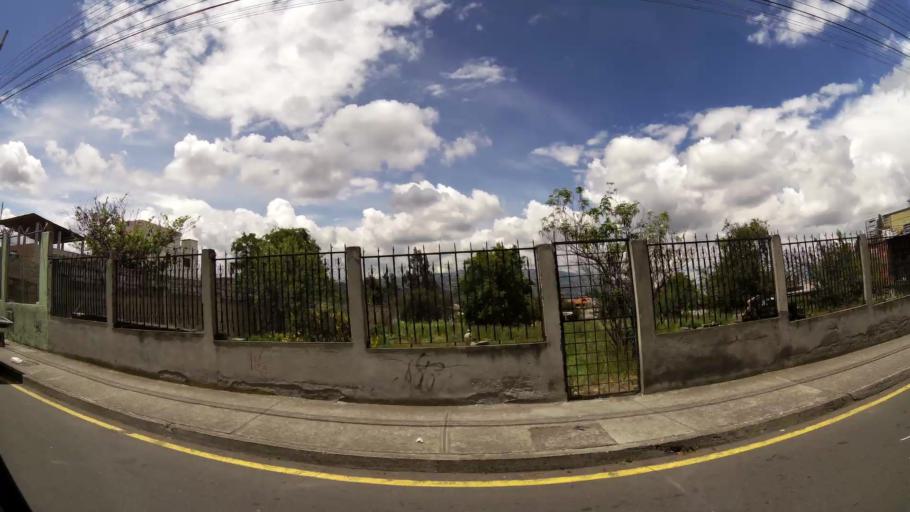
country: EC
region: Tungurahua
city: Ambato
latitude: -1.2751
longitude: -78.6215
